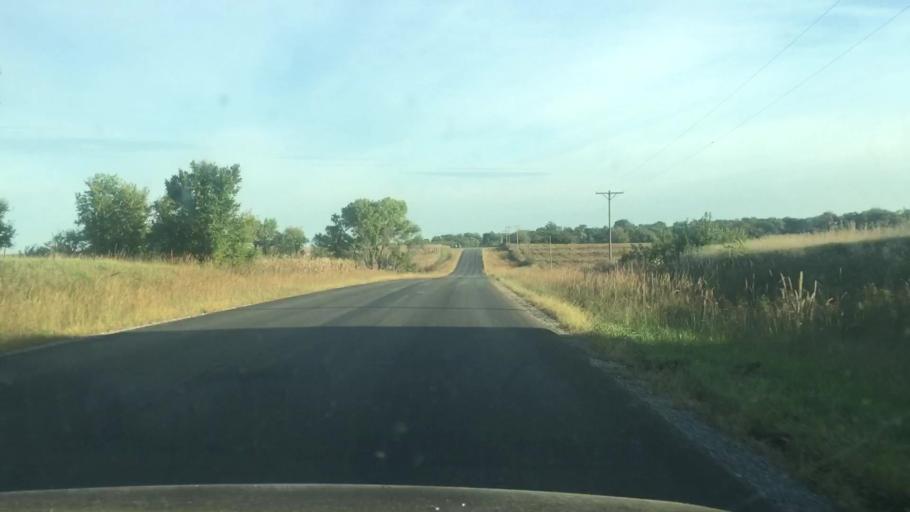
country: US
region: Kansas
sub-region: Marshall County
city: Marysville
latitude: 39.9538
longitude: -96.6009
